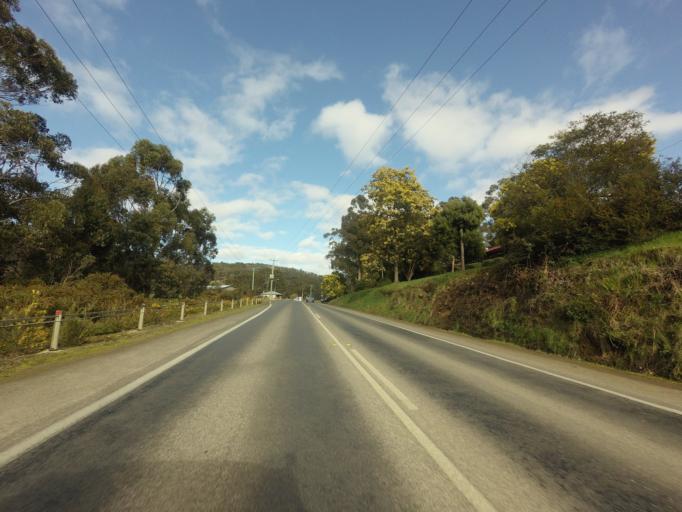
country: AU
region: Tasmania
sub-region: Huon Valley
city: Geeveston
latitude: -43.1654
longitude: 146.9446
